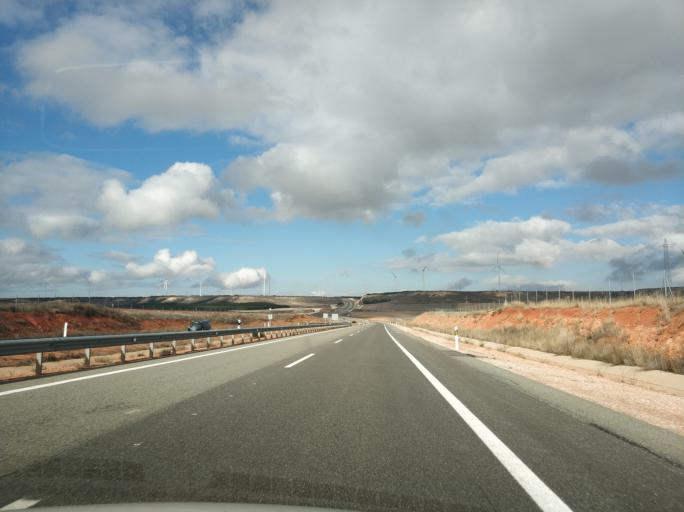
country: ES
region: Castille and Leon
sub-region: Provincia de Soria
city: Alcubilla de las Penas
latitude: 41.2724
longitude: -2.4743
